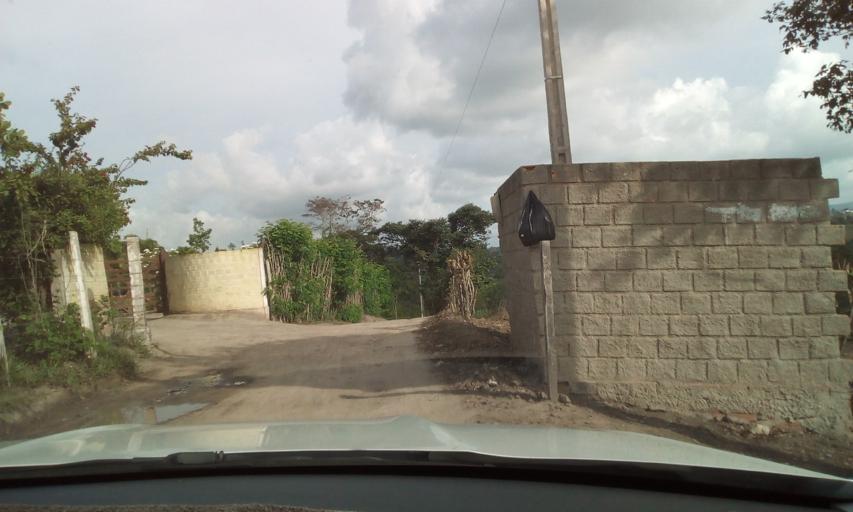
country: BR
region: Pernambuco
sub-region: Cha Grande
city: Cha Grande
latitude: -8.1969
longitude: -35.4947
